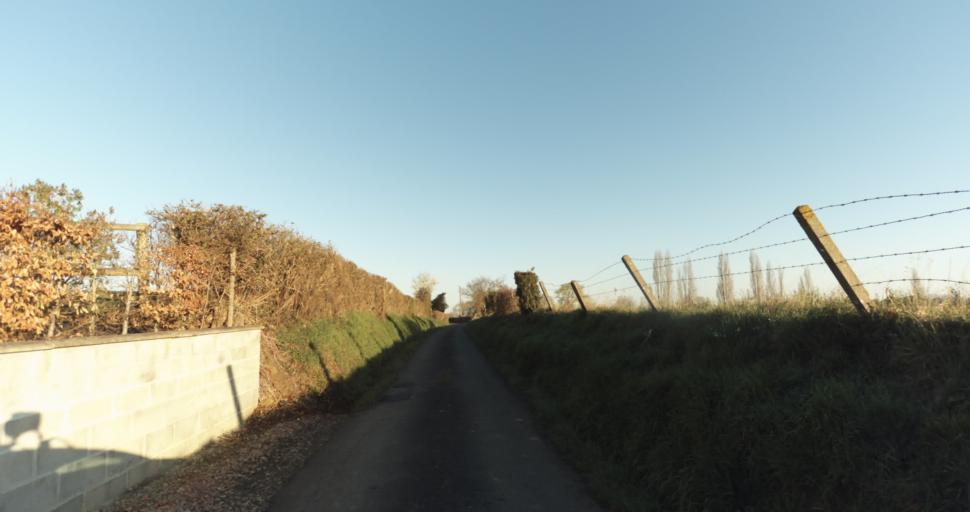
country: FR
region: Lower Normandy
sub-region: Departement du Calvados
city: Saint-Pierre-sur-Dives
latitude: 49.0244
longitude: -0.0117
